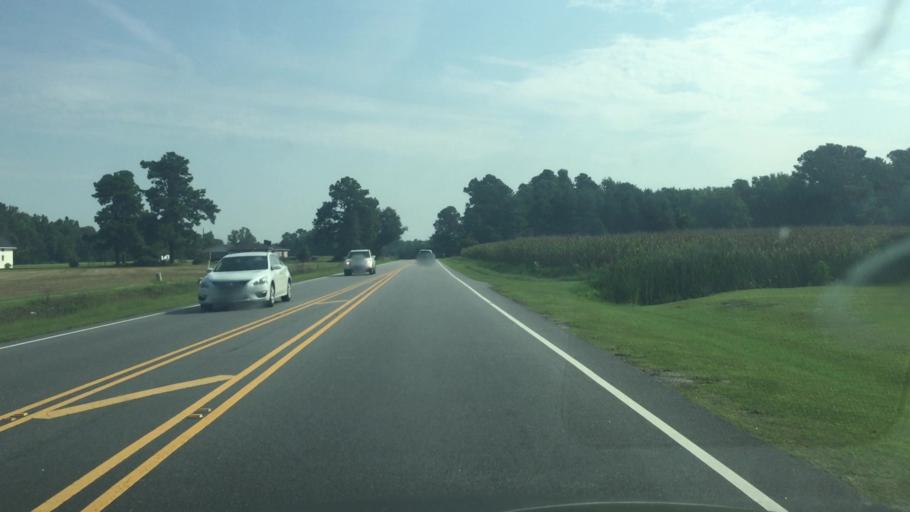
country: US
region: North Carolina
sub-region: Columbus County
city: Tabor City
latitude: 34.2036
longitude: -78.8302
